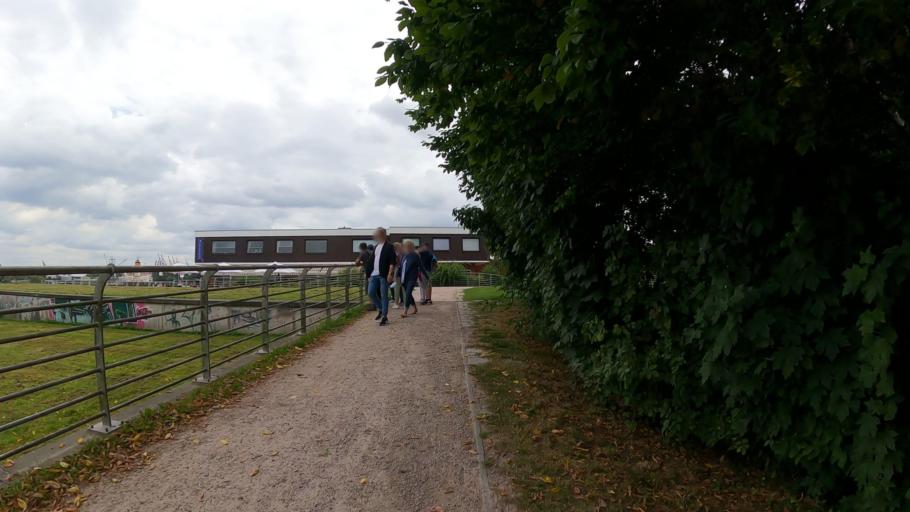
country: DE
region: Hamburg
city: Altona
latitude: 53.5390
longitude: 9.8731
